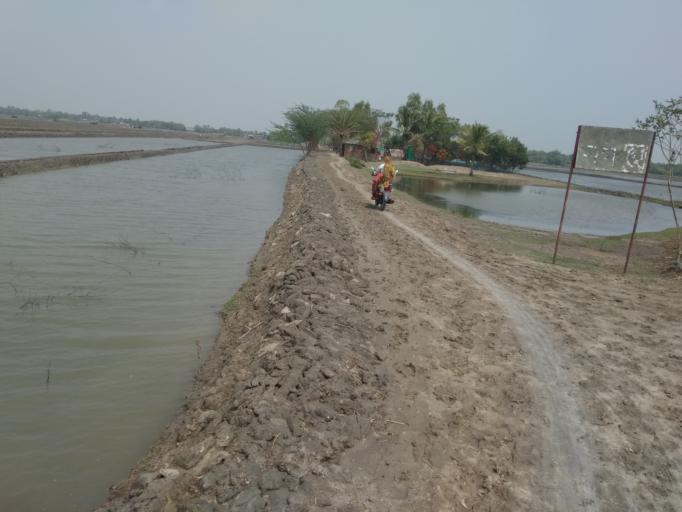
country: IN
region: West Bengal
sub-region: North 24 Parganas
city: Taki
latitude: 22.2749
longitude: 89.2841
